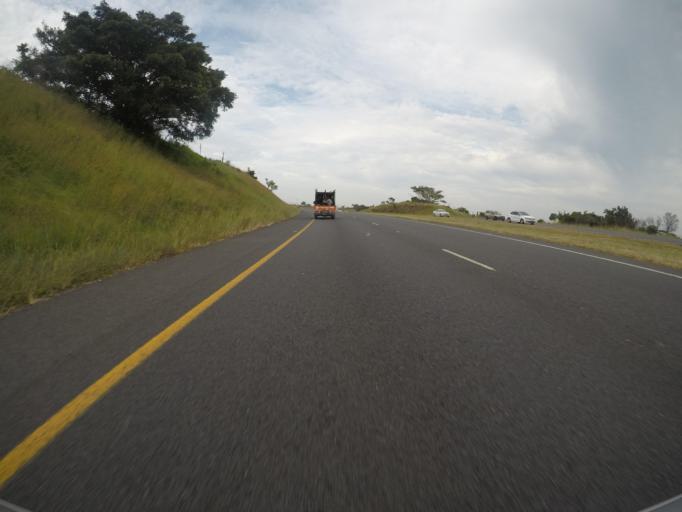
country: ZA
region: Eastern Cape
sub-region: Buffalo City Metropolitan Municipality
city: East London
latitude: -32.9683
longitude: 27.8744
